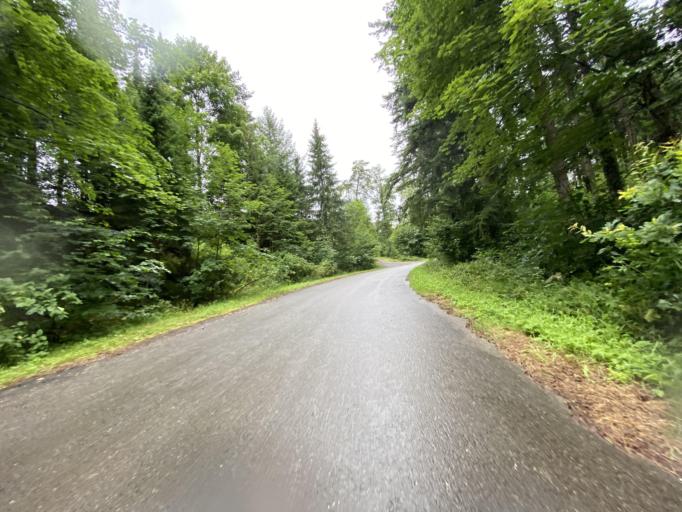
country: DE
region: Baden-Wuerttemberg
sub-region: Tuebingen Region
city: Sigmaringen
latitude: 48.1112
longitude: 9.2424
